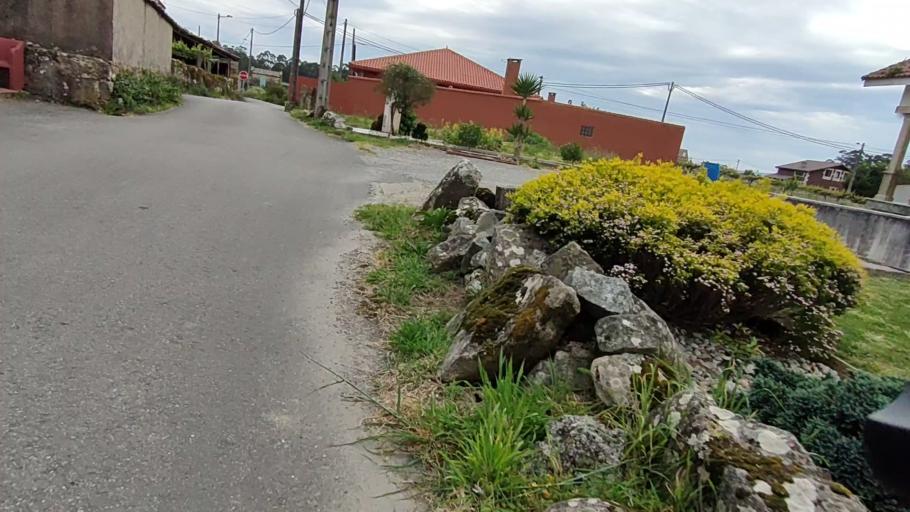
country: ES
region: Galicia
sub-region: Provincia da Coruna
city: Boiro
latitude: 42.6341
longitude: -8.8653
